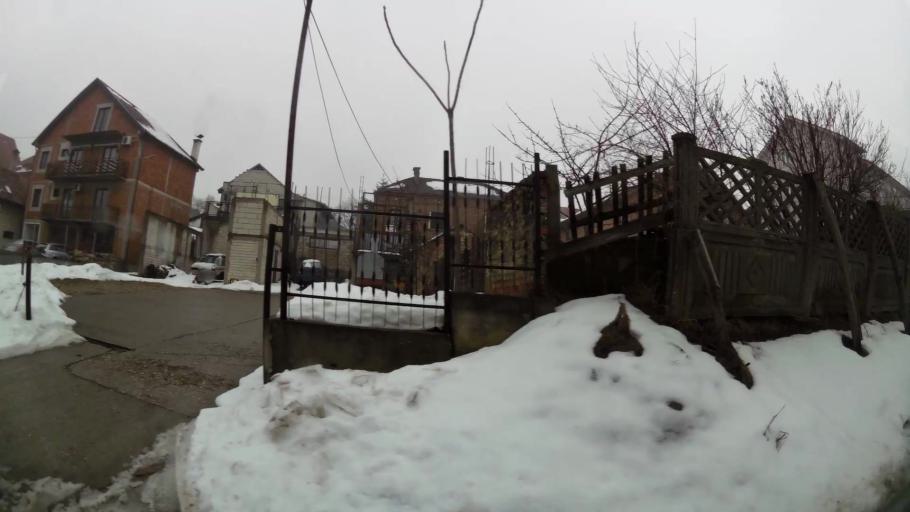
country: RS
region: Central Serbia
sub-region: Belgrade
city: Zvezdara
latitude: 44.7789
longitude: 20.5256
